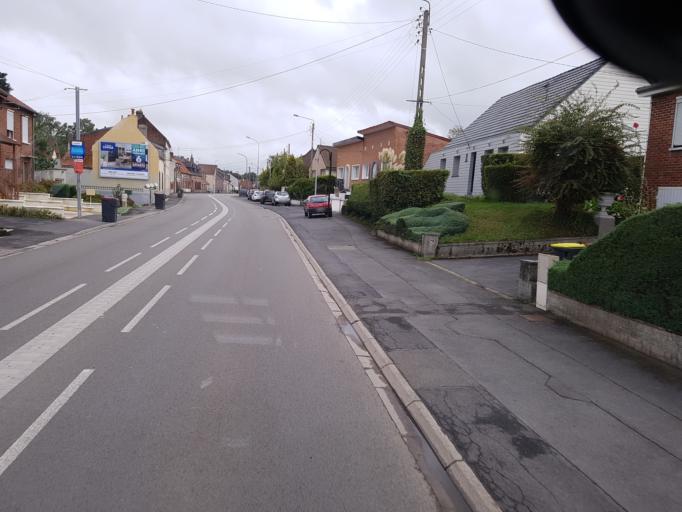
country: FR
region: Nord-Pas-de-Calais
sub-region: Departement du Pas-de-Calais
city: Souchez
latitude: 50.3968
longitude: 2.7493
